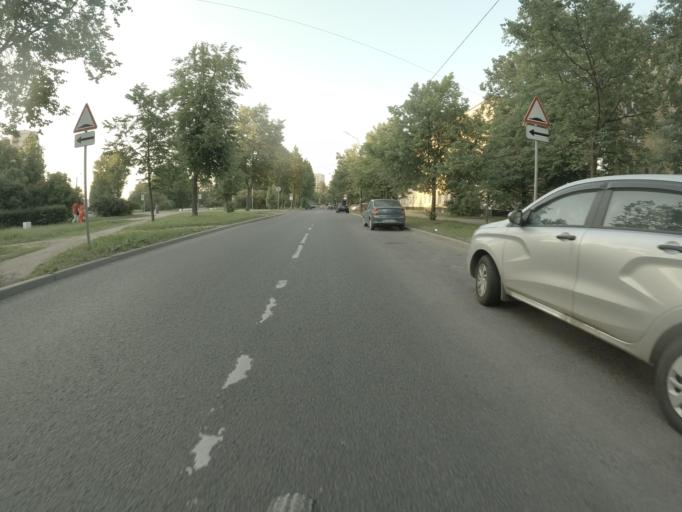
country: RU
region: St.-Petersburg
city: Dachnoye
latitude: 59.8449
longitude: 30.2679
